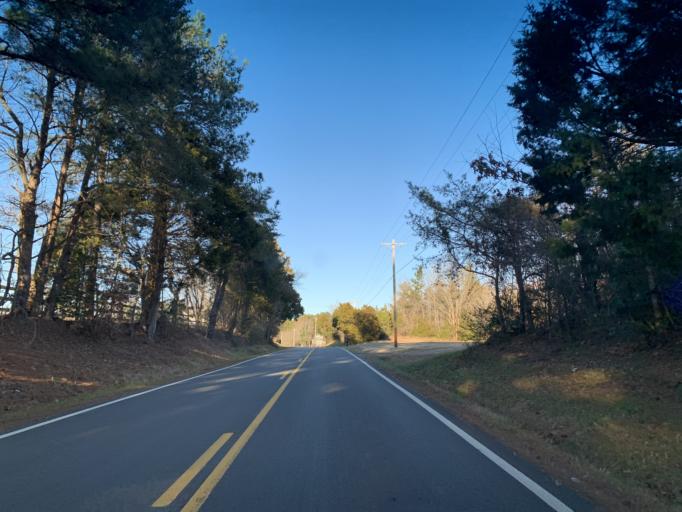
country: US
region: Maryland
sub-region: Saint Mary's County
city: Mechanicsville
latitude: 38.4265
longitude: -76.6878
